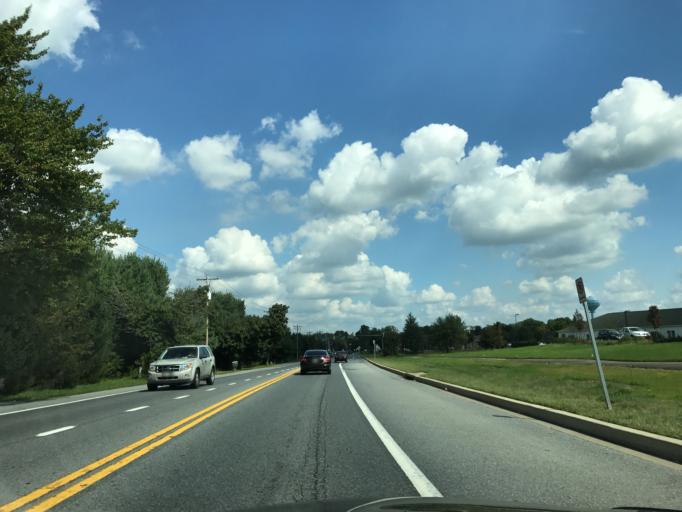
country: US
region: Maryland
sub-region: Queen Anne's County
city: Centreville
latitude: 39.0321
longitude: -76.0768
